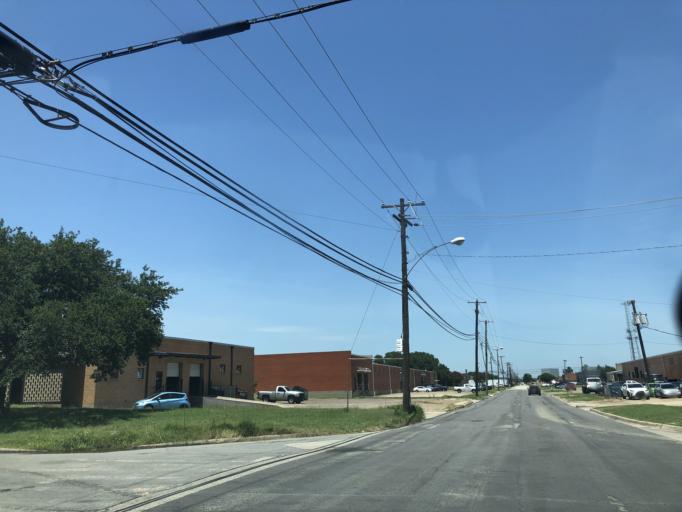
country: US
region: Texas
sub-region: Dallas County
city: Irving
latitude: 32.8168
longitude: -96.8886
